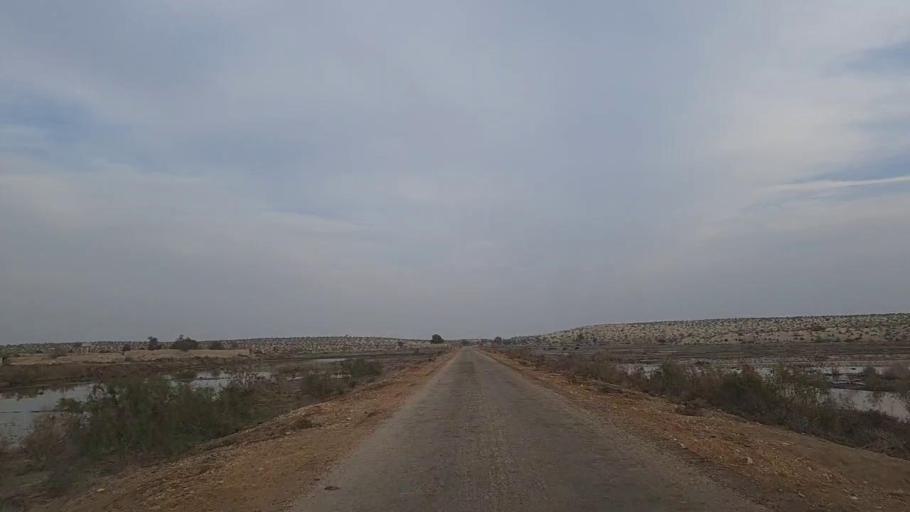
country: PK
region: Sindh
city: Daur
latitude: 26.5156
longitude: 68.4897
